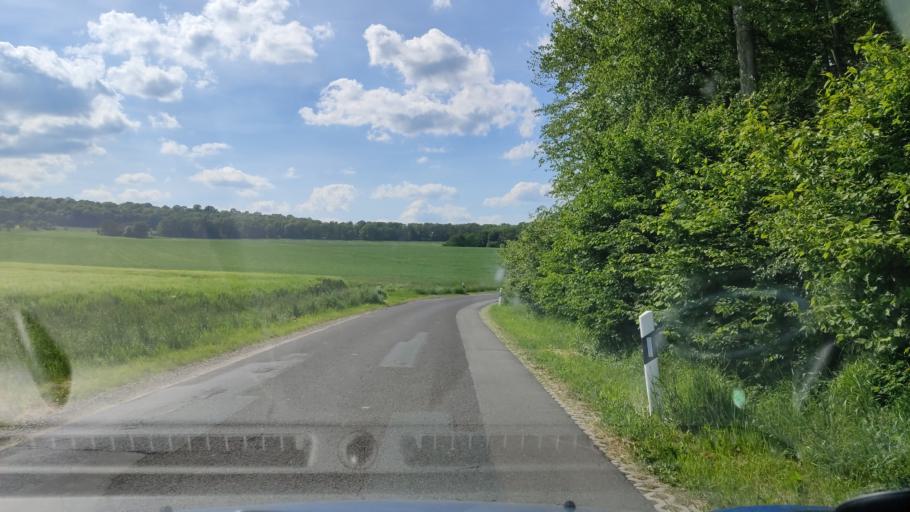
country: DE
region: Lower Saxony
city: Dransfeld
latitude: 51.5407
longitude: 9.8076
